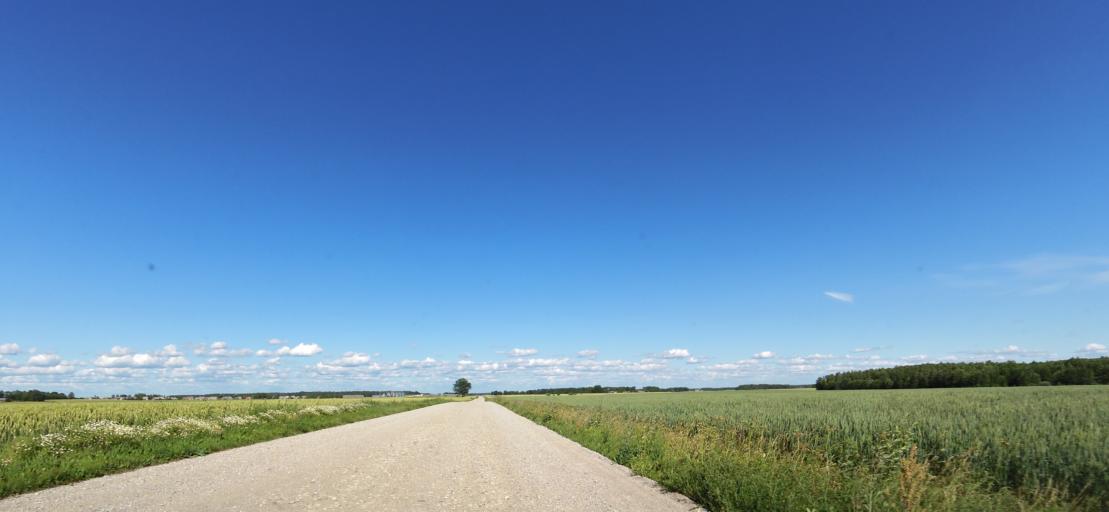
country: LT
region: Panevezys
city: Pasvalys
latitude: 56.1241
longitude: 24.3731
